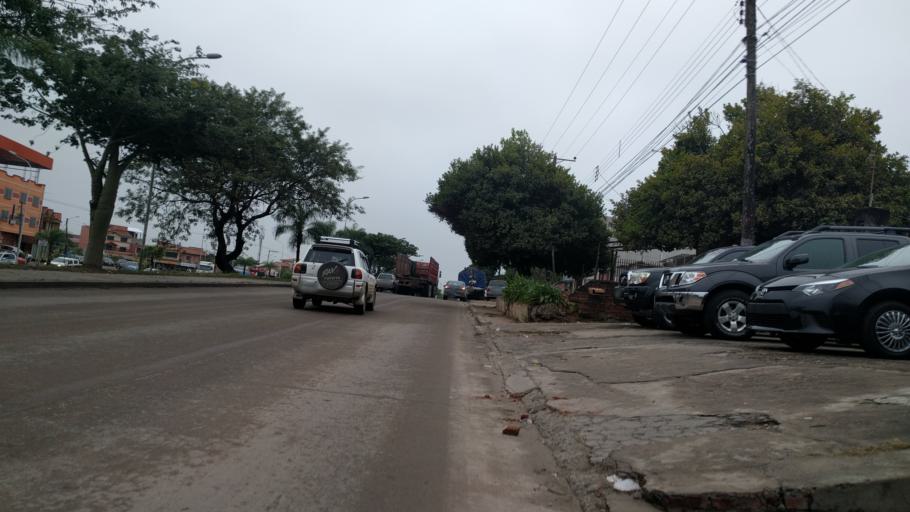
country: BO
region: Santa Cruz
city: Santa Cruz de la Sierra
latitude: -17.8173
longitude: -63.2018
